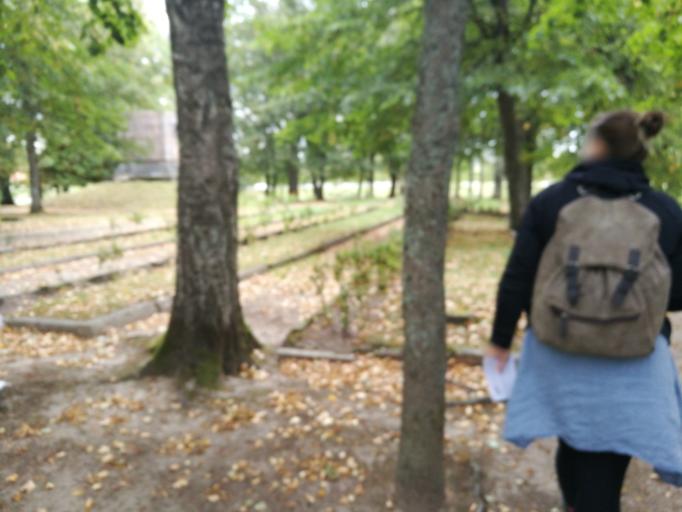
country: LV
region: Limbazu Rajons
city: Limbazi
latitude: 57.5159
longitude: 24.7178
